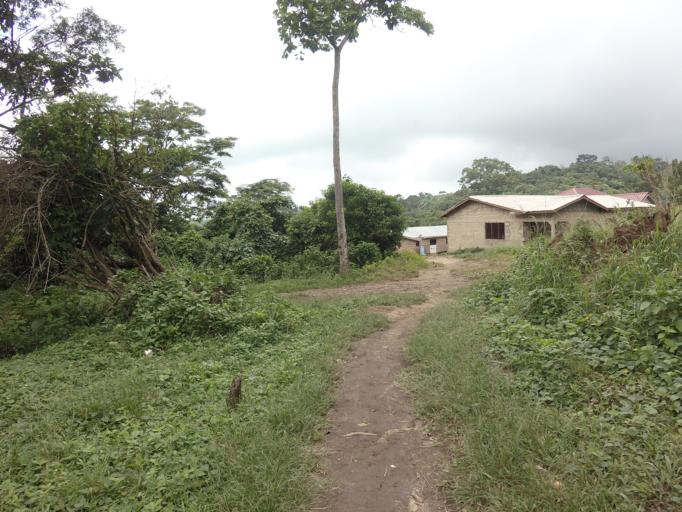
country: TG
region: Plateaux
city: Kpalime
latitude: 6.8457
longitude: 0.4423
